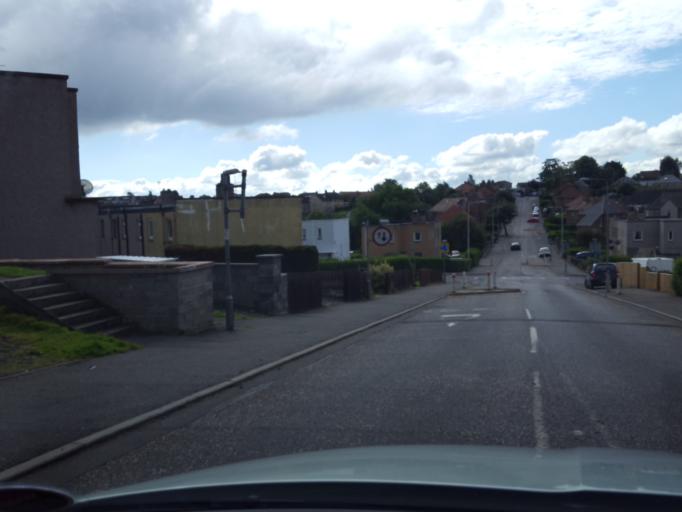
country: GB
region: Scotland
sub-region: Fife
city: Townhill
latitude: 56.0644
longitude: -3.4364
